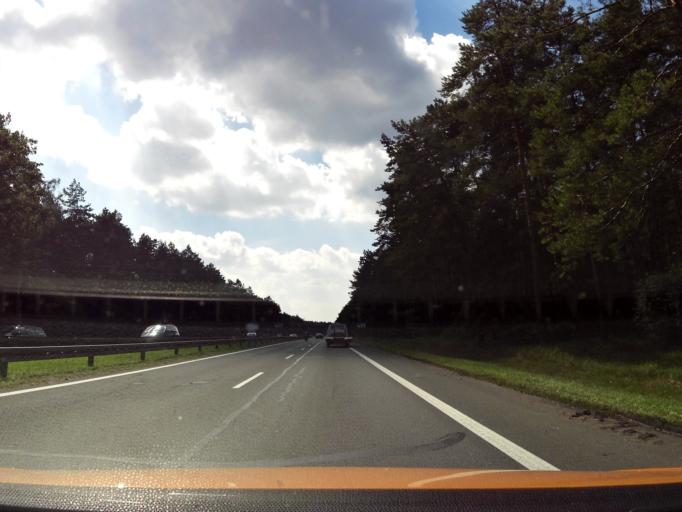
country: PL
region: West Pomeranian Voivodeship
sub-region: Powiat stargardzki
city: Kobylanka
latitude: 53.4296
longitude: 14.7729
